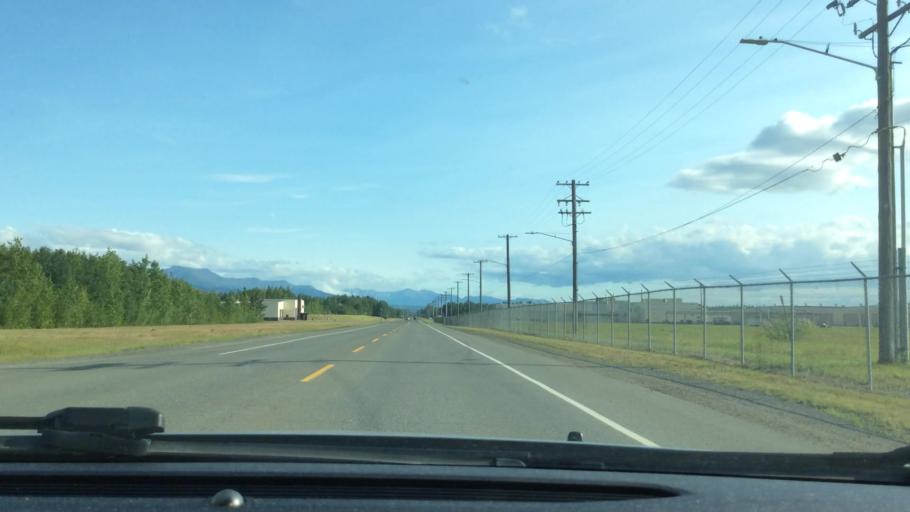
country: US
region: Alaska
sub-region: Anchorage Municipality
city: Anchorage
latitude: 61.2497
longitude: -149.7794
